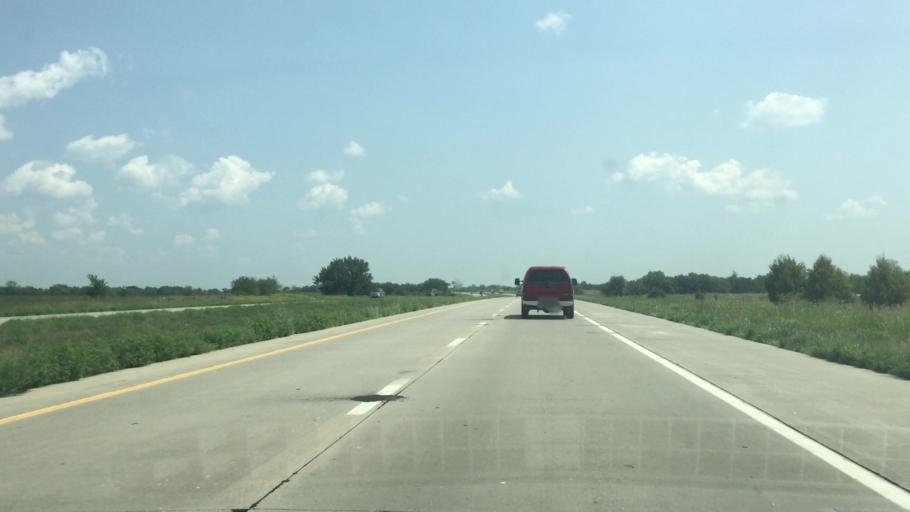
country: US
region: Kansas
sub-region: Franklin County
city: Wellsville
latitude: 38.6774
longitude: -95.1365
